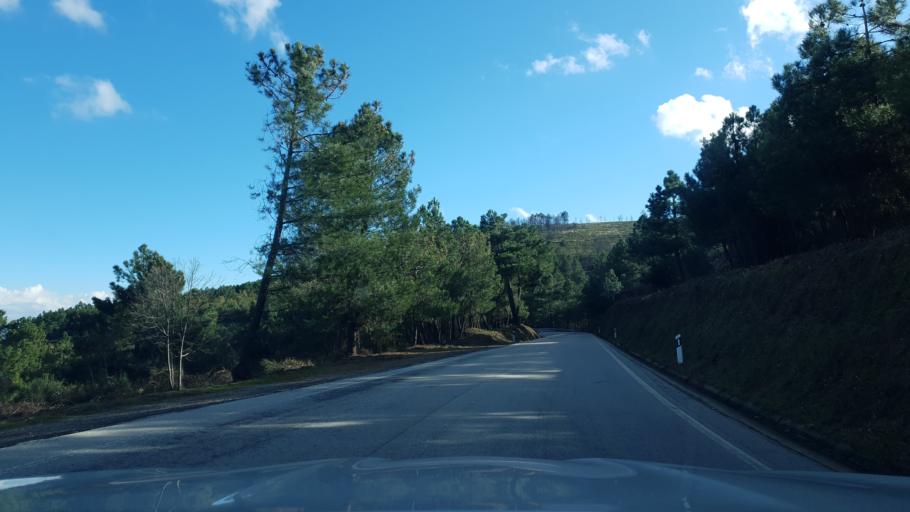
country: PT
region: Braganca
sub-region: Torre de Moncorvo
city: Torre de Moncorvo
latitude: 41.1842
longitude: -6.9442
